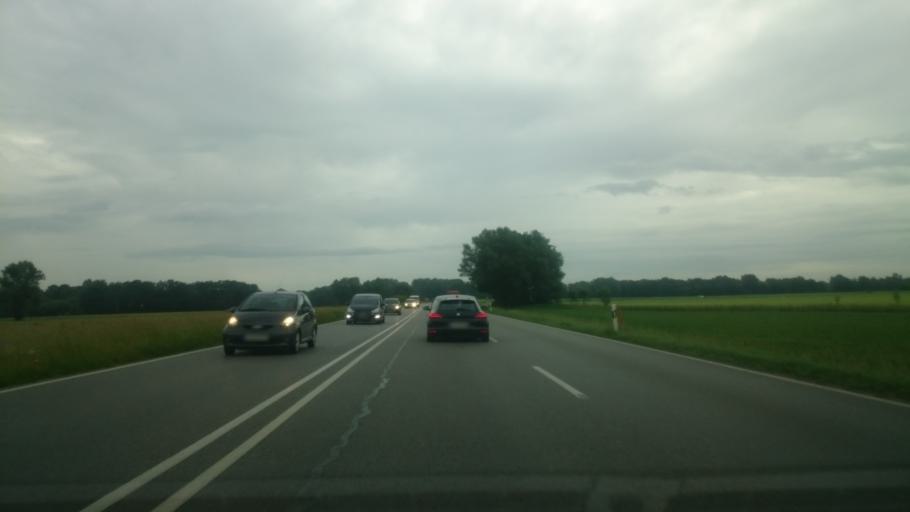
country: DE
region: Bavaria
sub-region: Upper Bavaria
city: Pornbach
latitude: 48.6273
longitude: 11.4447
